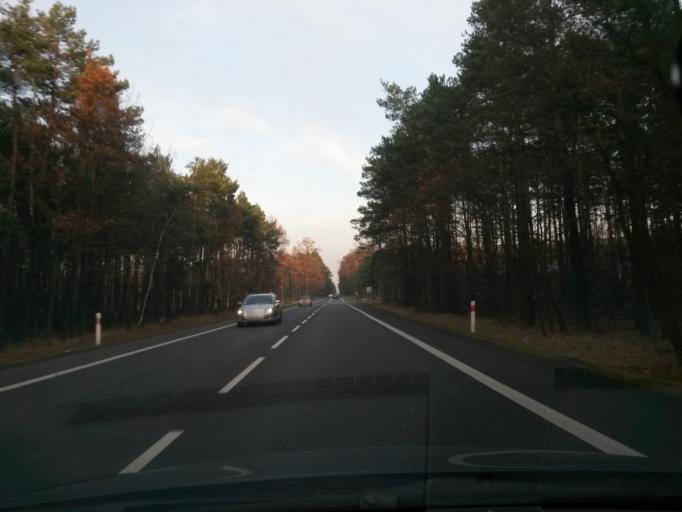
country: PL
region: Lodz Voivodeship
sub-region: Powiat wielunski
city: Wierzchlas
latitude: 51.2529
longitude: 18.7181
